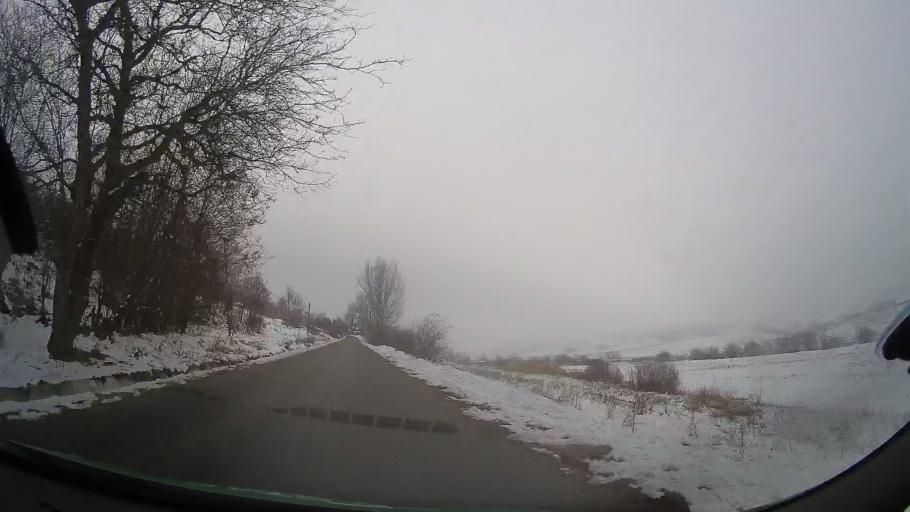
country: RO
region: Bacau
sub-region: Comuna Vultureni
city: Vultureni
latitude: 46.3081
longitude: 27.2929
